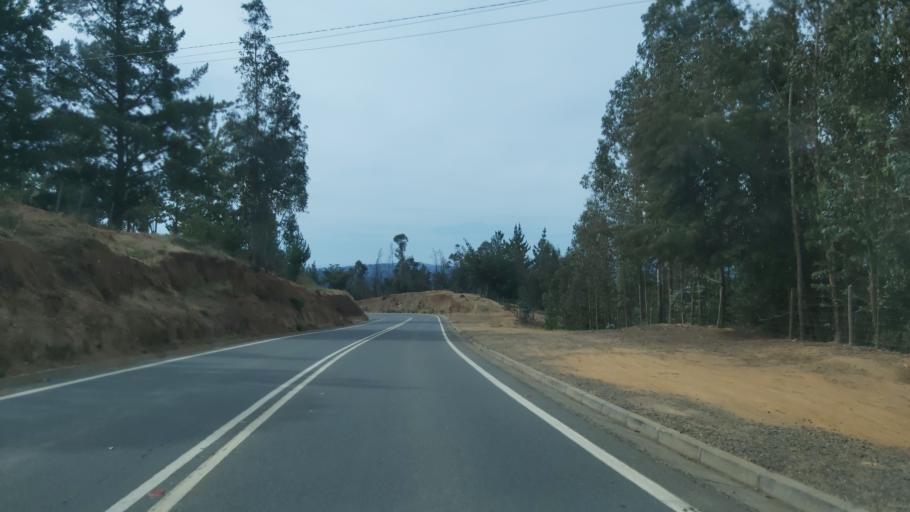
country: CL
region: Maule
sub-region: Provincia de Talca
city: Constitucion
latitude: -34.9172
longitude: -71.9926
